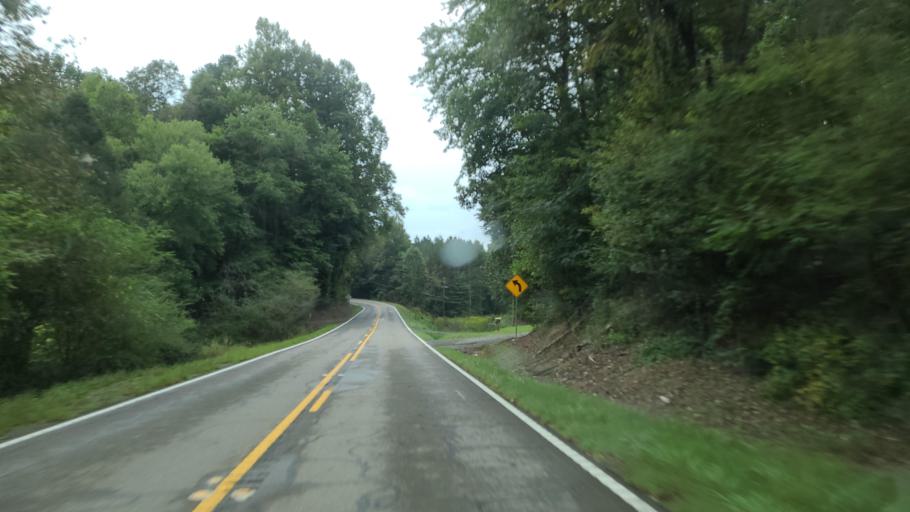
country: US
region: Georgia
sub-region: Gilmer County
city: Ellijay
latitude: 34.7432
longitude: -84.5278
